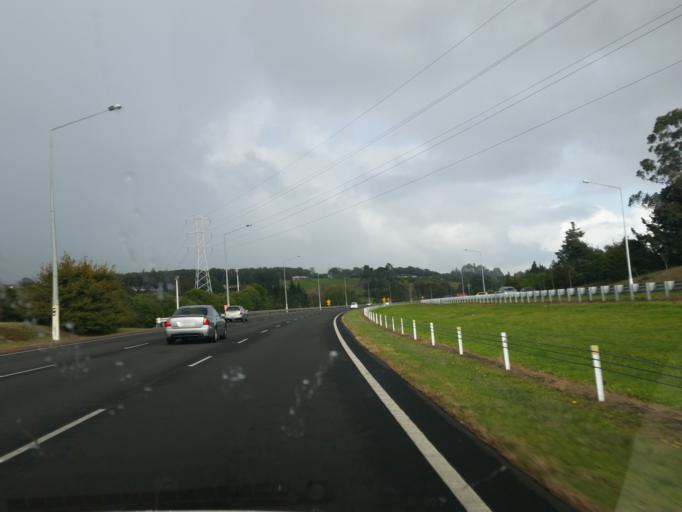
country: NZ
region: Auckland
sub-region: Auckland
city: Pukekohe East
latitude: -37.1679
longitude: 174.9846
